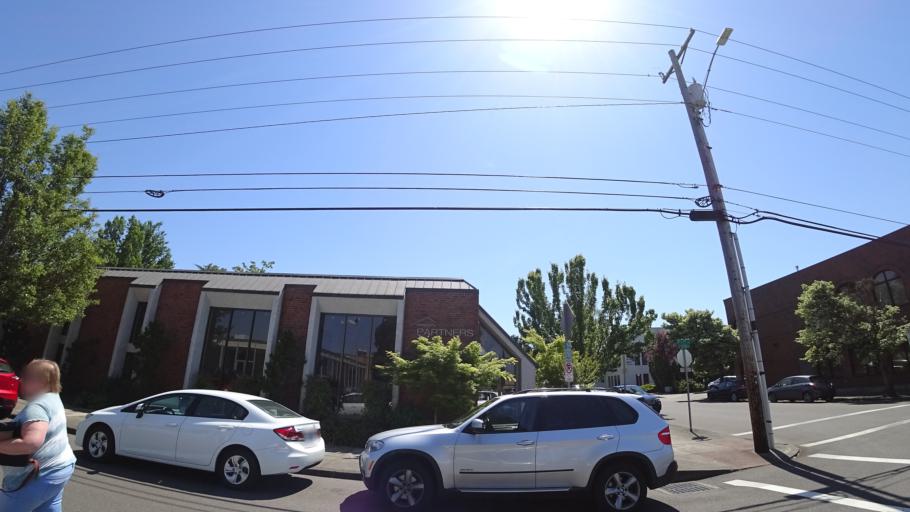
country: US
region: Oregon
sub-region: Washington County
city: Beaverton
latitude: 45.4860
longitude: -122.8020
